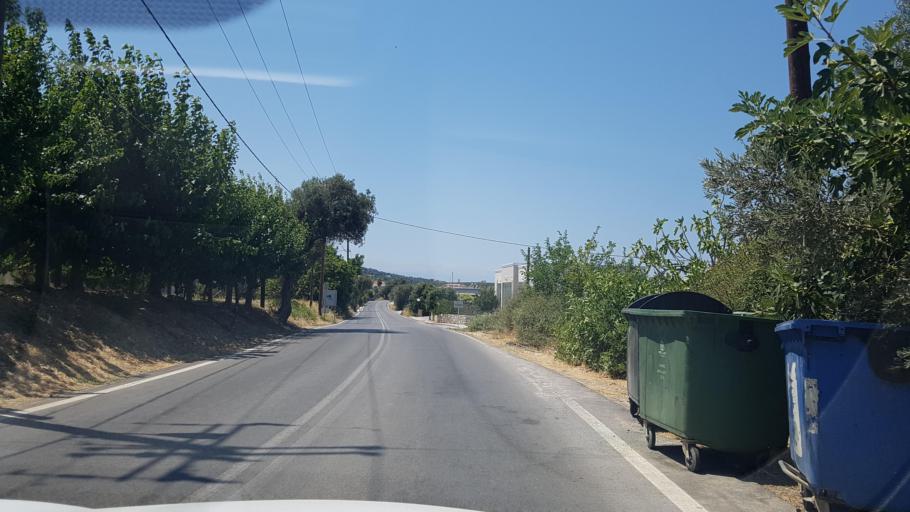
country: GR
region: Crete
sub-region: Nomos Rethymnis
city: Rethymno
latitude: 35.3588
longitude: 24.5708
